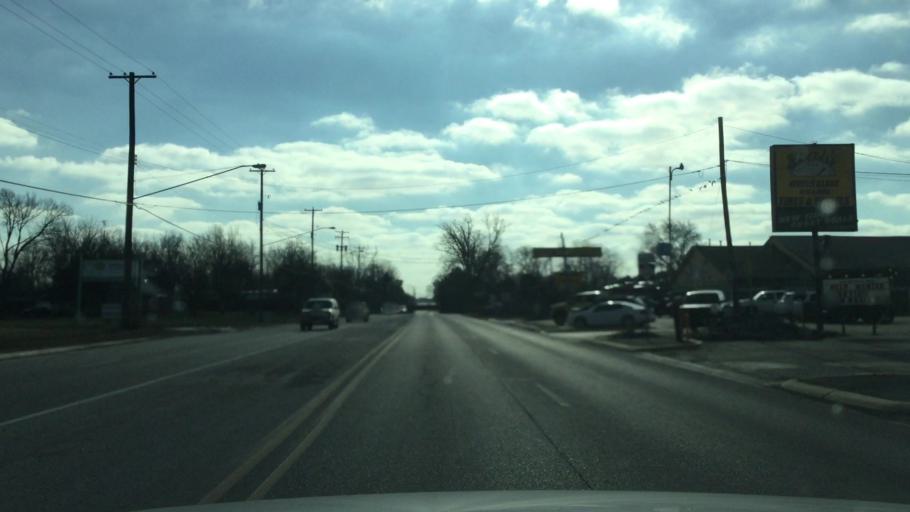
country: US
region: Michigan
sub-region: Genesee County
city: Beecher
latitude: 43.0683
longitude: -83.6741
